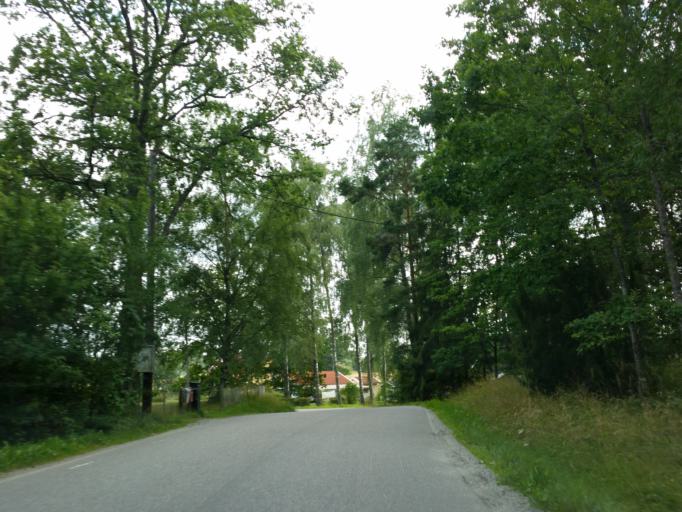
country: SE
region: Soedermanland
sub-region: Strangnas Kommun
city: Mariefred
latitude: 59.2243
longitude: 17.3071
